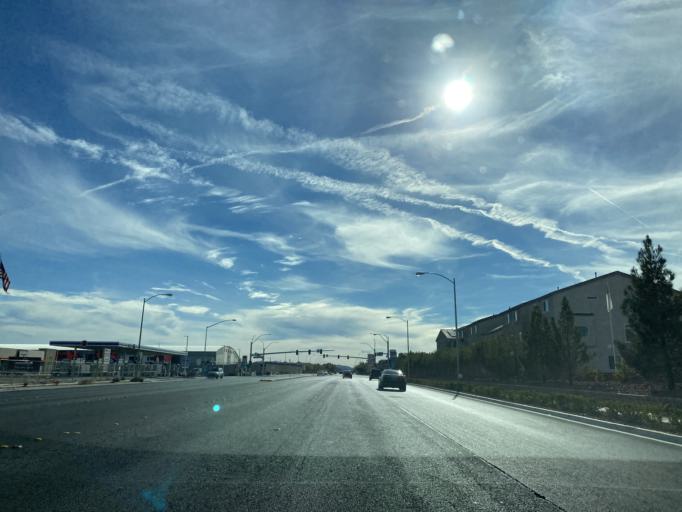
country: US
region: Nevada
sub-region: Clark County
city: Enterprise
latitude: 36.0581
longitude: -115.2249
